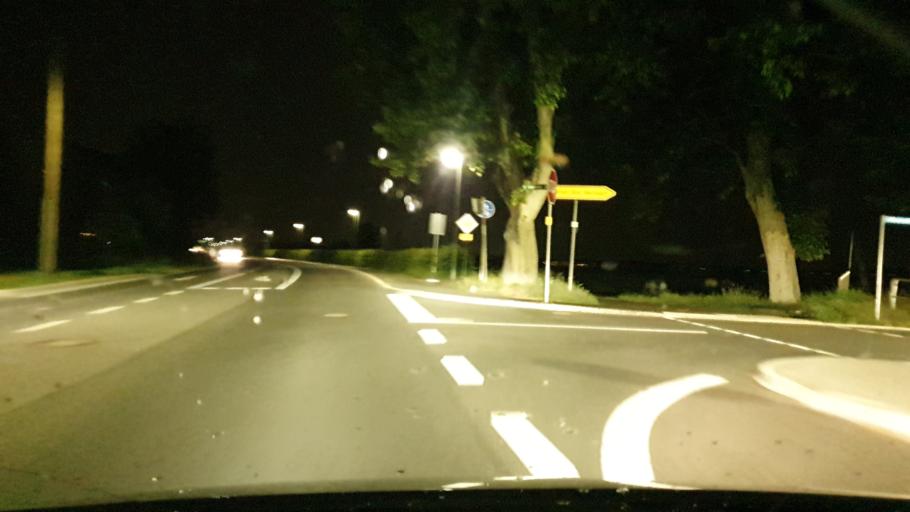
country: DE
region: Hesse
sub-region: Regierungsbezirk Darmstadt
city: Florsheim
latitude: 50.0312
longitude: 8.4347
